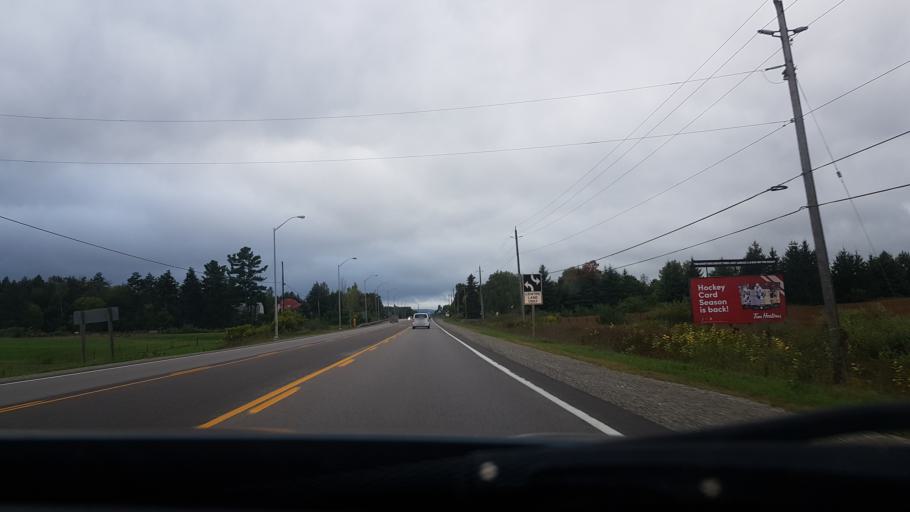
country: CA
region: Ontario
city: Bradford West Gwillimbury
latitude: 43.9760
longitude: -79.8387
